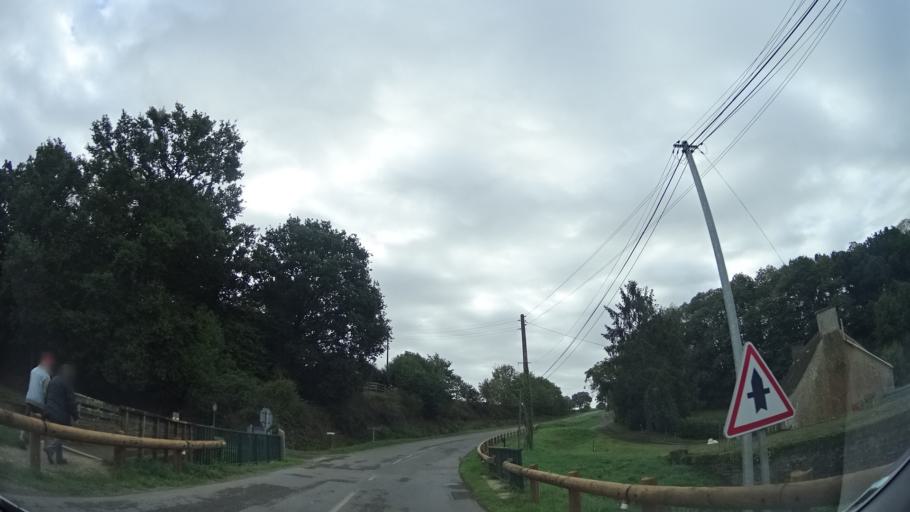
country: FR
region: Brittany
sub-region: Departement d'Ille-et-Vilaine
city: Montreuil-sur-Ille
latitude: 48.3365
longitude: -1.6499
